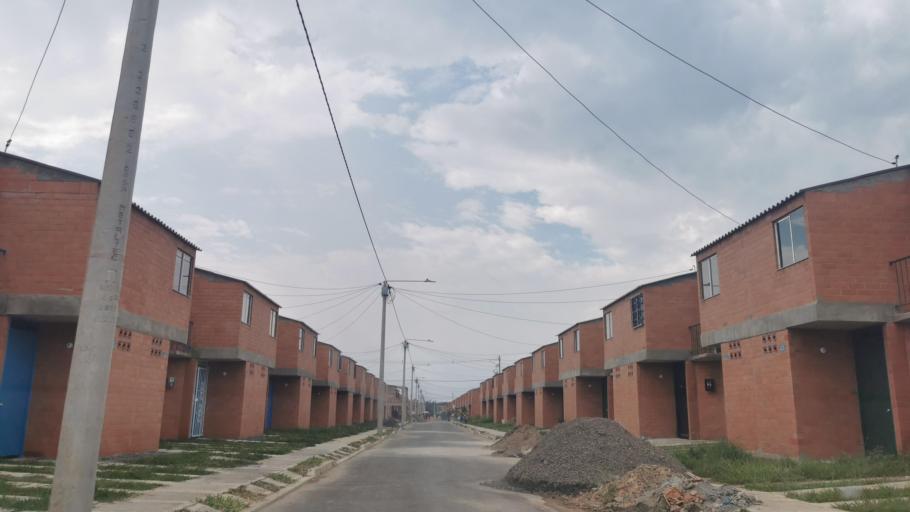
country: CO
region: Valle del Cauca
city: Jamundi
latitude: 3.2323
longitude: -76.5250
